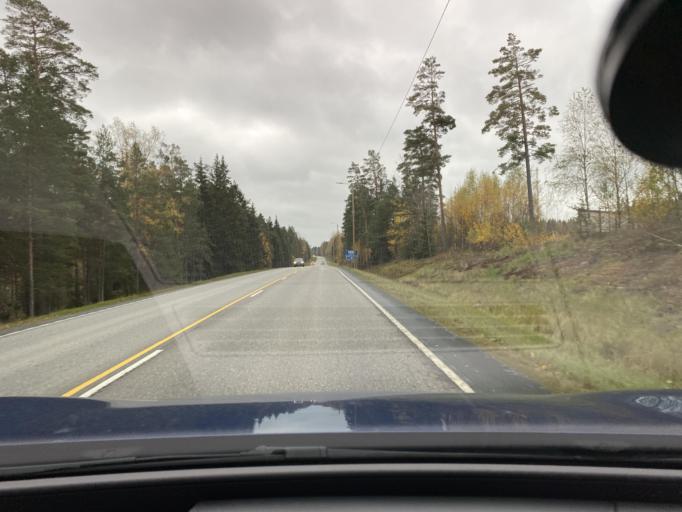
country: FI
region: Varsinais-Suomi
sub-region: Vakka-Suomi
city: Laitila
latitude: 60.9669
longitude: 21.5941
